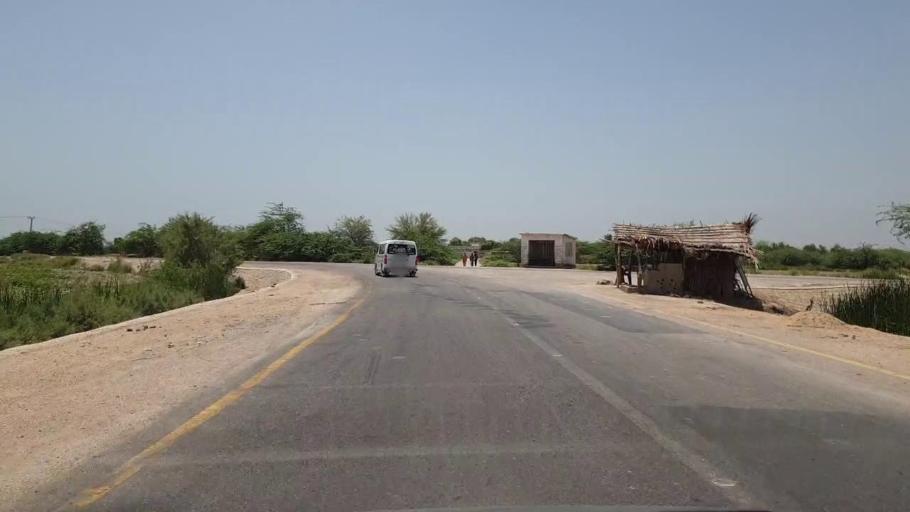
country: PK
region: Sindh
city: Sakrand
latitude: 26.1109
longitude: 68.3891
